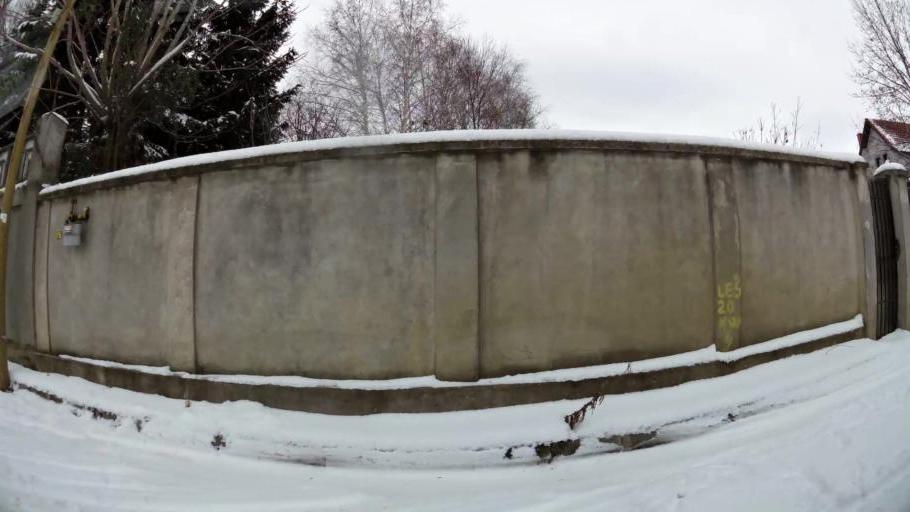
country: RO
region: Ilfov
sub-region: Comuna Tunari
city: Tunari
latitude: 44.5190
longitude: 26.1459
